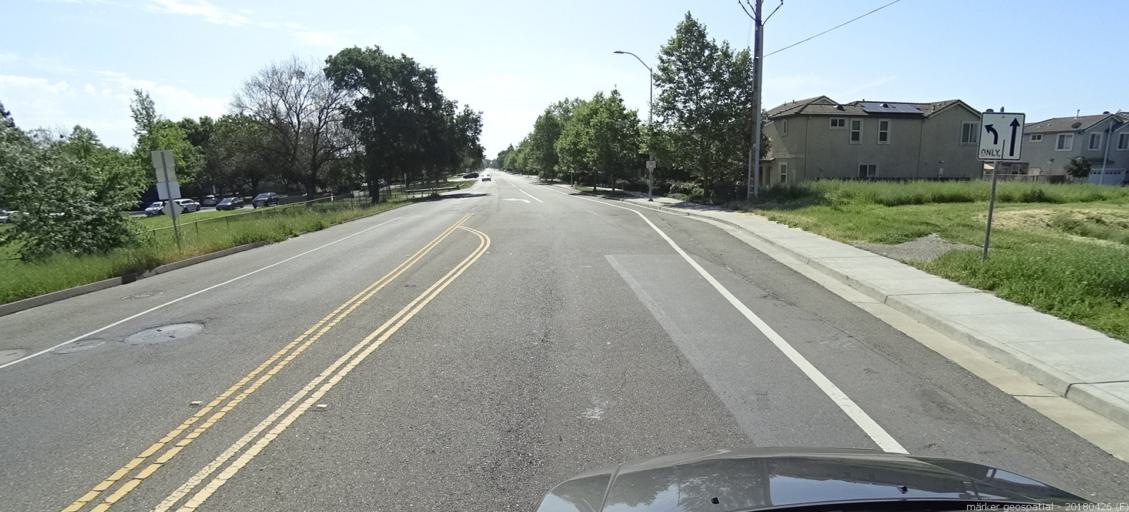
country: US
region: California
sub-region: Yolo County
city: West Sacramento
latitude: 38.5478
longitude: -121.5354
